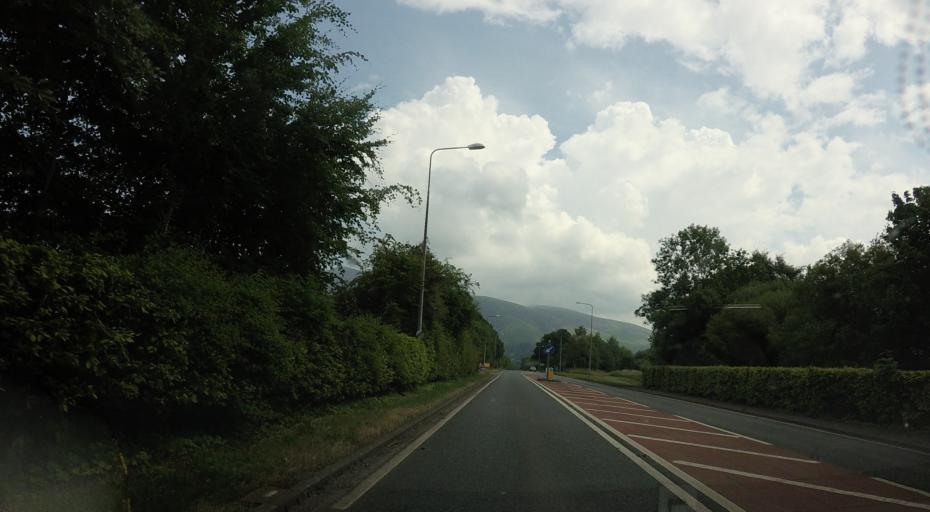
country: GB
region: England
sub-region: Cumbria
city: Keswick
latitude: 54.6045
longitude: -3.1649
